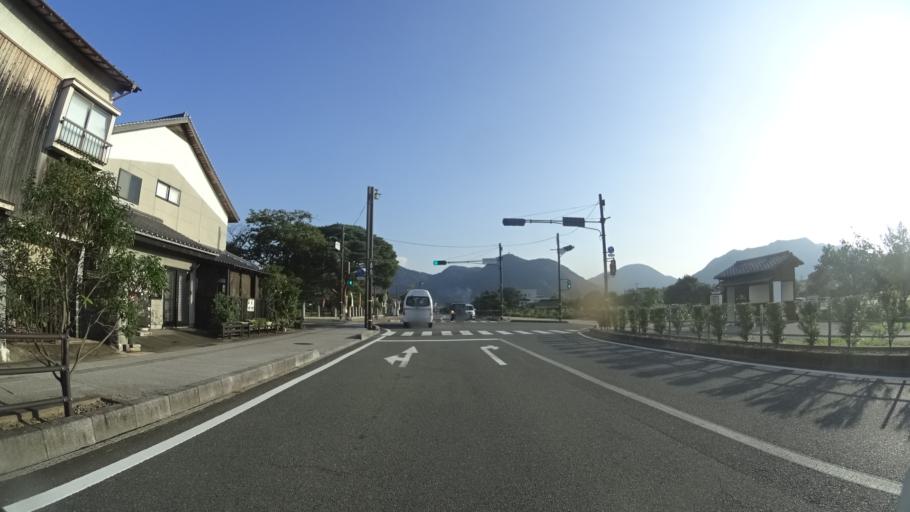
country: JP
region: Yamaguchi
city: Hagi
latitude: 34.4135
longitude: 131.3923
